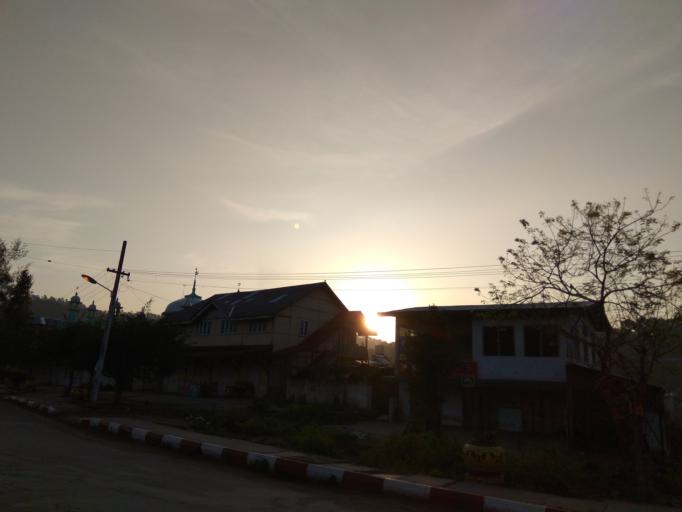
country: MM
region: Mandalay
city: Yamethin
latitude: 20.6332
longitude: 96.5660
